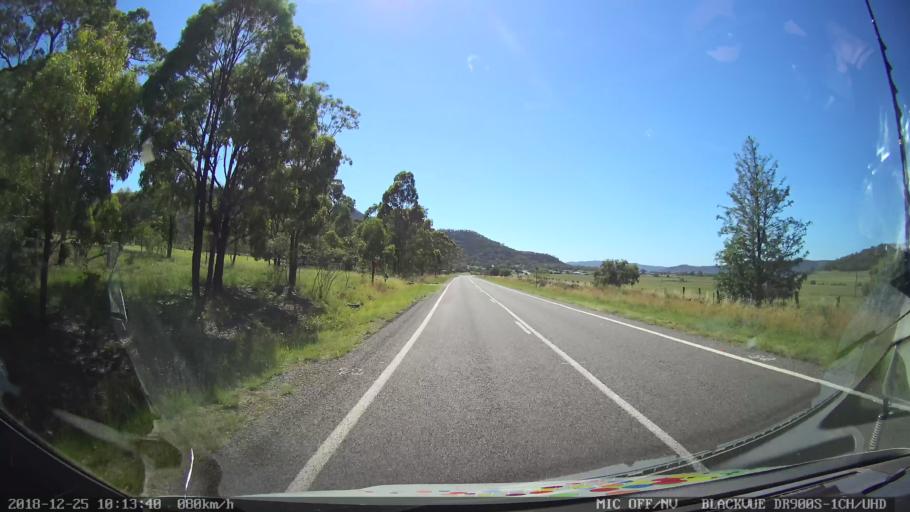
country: AU
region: New South Wales
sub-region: Muswellbrook
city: Denman
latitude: -32.3262
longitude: 150.5478
